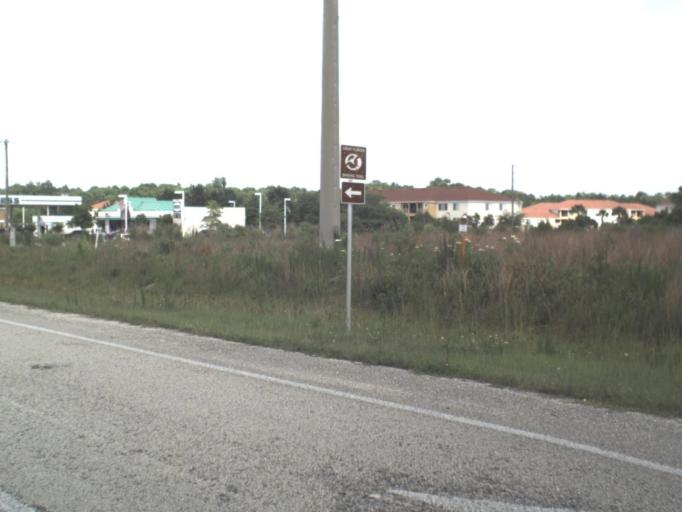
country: US
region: Florida
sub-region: Clay County
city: Lakeside
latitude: 30.1137
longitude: -81.8139
